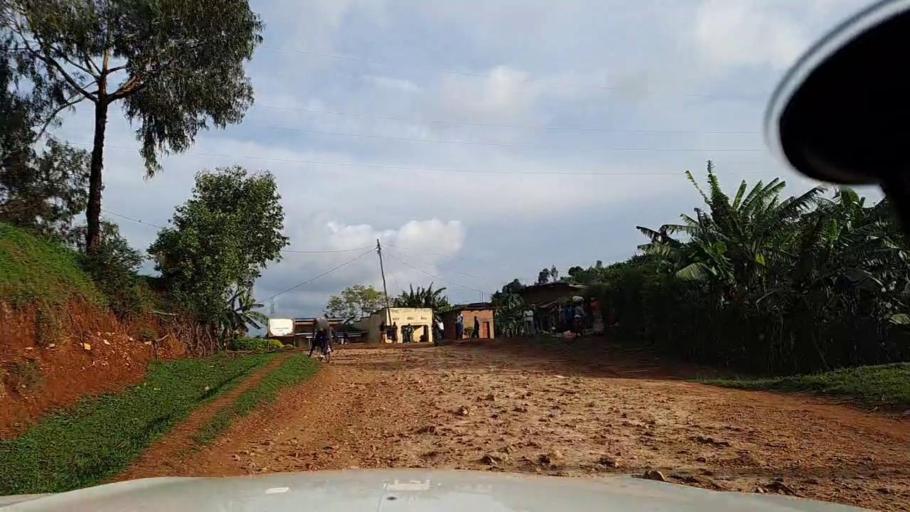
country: RW
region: Southern Province
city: Gitarama
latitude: -2.1857
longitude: 29.5645
